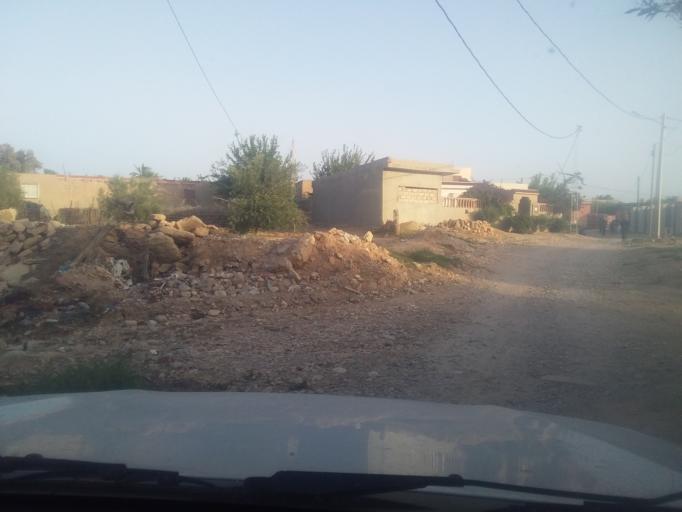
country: TN
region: Qabis
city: Gabes
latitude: 33.6258
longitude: 10.2920
